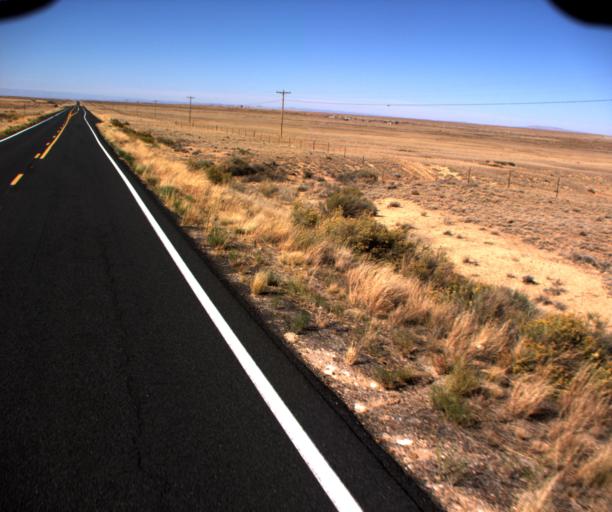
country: US
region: Arizona
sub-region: Coconino County
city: Tuba City
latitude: 35.9958
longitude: -111.0250
